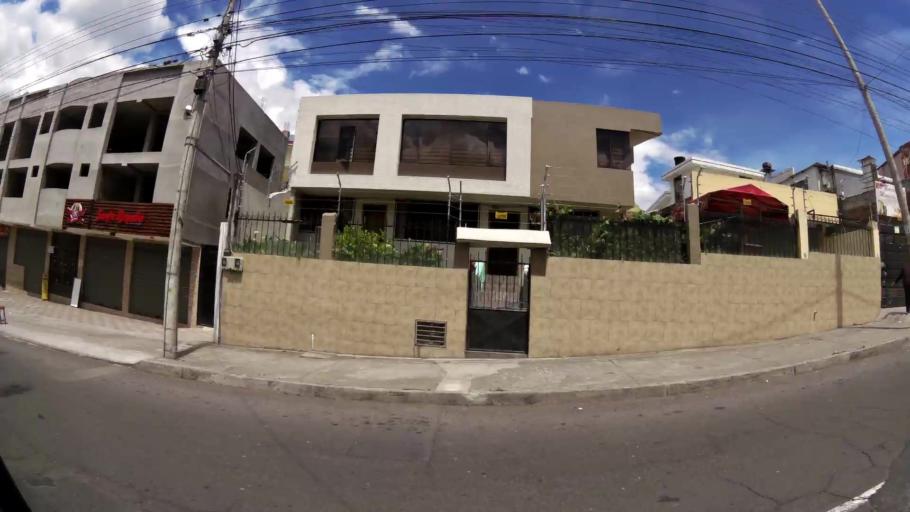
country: EC
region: Tungurahua
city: Ambato
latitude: -1.2594
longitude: -78.6400
